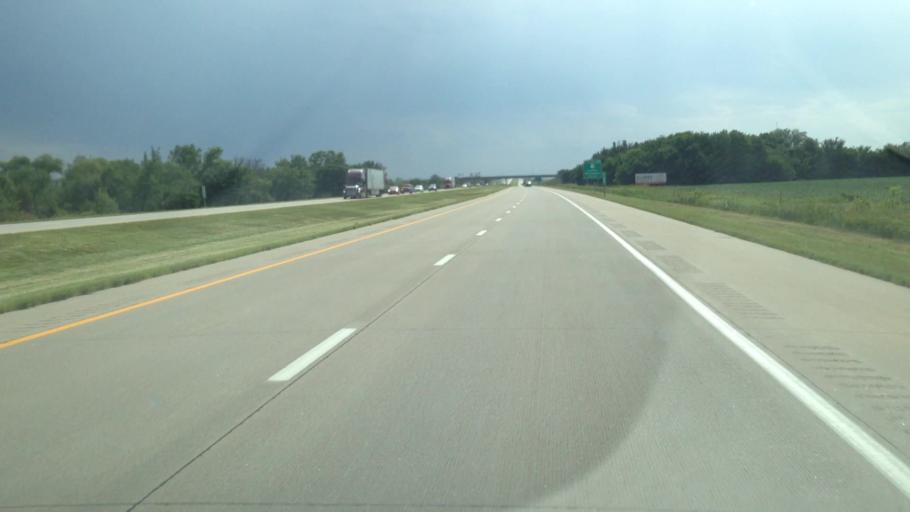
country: US
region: Kansas
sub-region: Osage County
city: Lyndon
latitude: 38.4363
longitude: -95.7018
